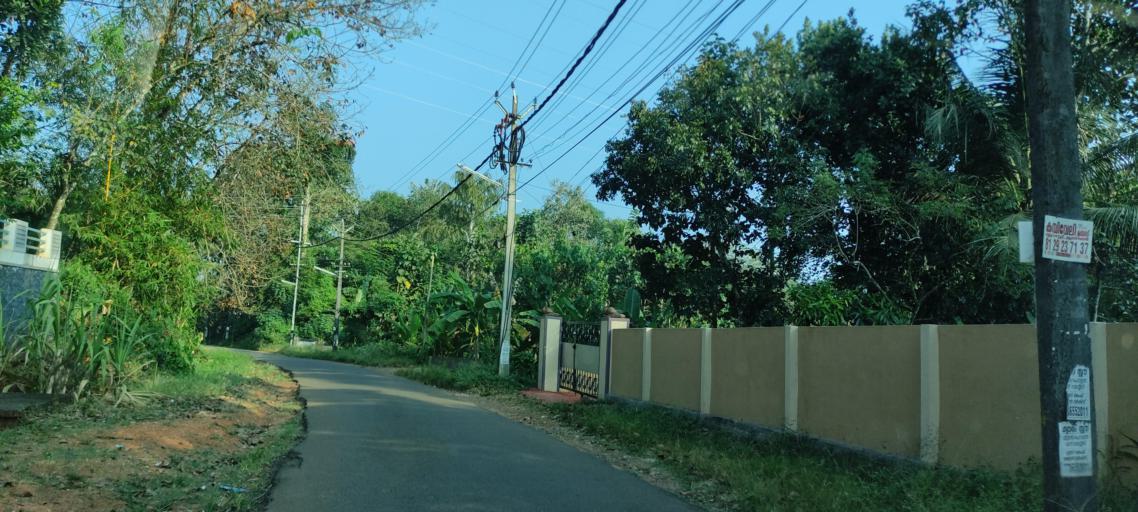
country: IN
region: Kerala
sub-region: Pattanamtitta
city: Adur
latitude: 9.1527
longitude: 76.7518
